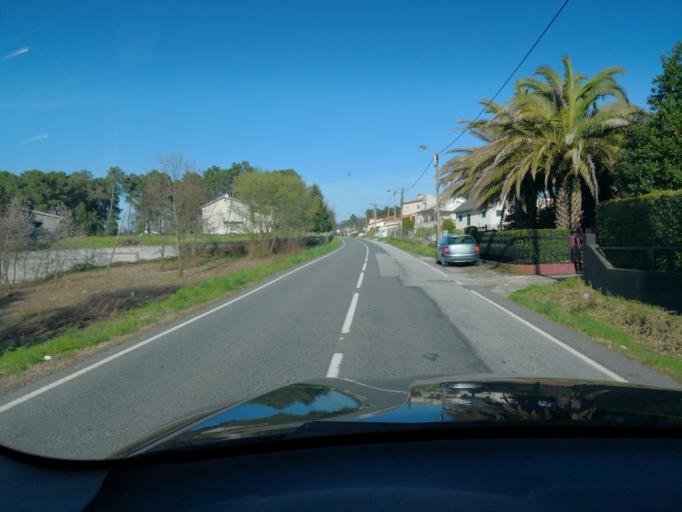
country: PT
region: Vila Real
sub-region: Vila Real
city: Vila Real
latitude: 41.3228
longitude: -7.6909
